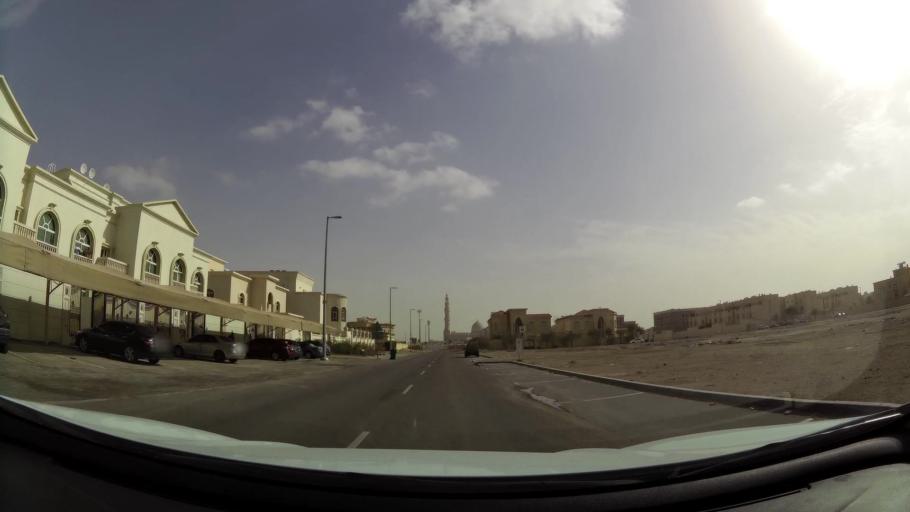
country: AE
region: Abu Dhabi
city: Abu Dhabi
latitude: 24.4315
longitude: 54.5925
